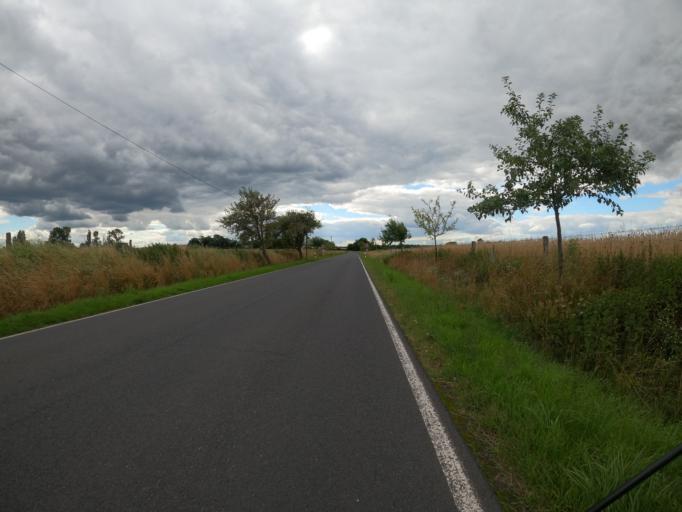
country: DE
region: Brandenburg
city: Angermunde
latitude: 53.0371
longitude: 13.9816
